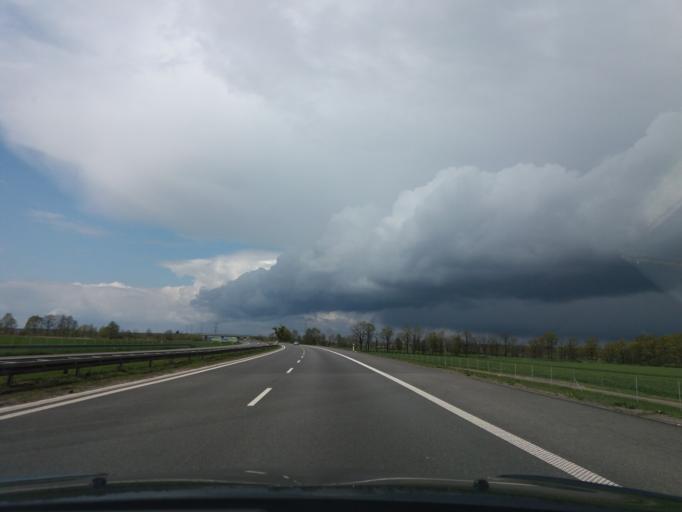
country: PL
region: Opole Voivodeship
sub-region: Powiat brzeski
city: Lewin Brzeski
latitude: 50.7069
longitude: 17.6102
